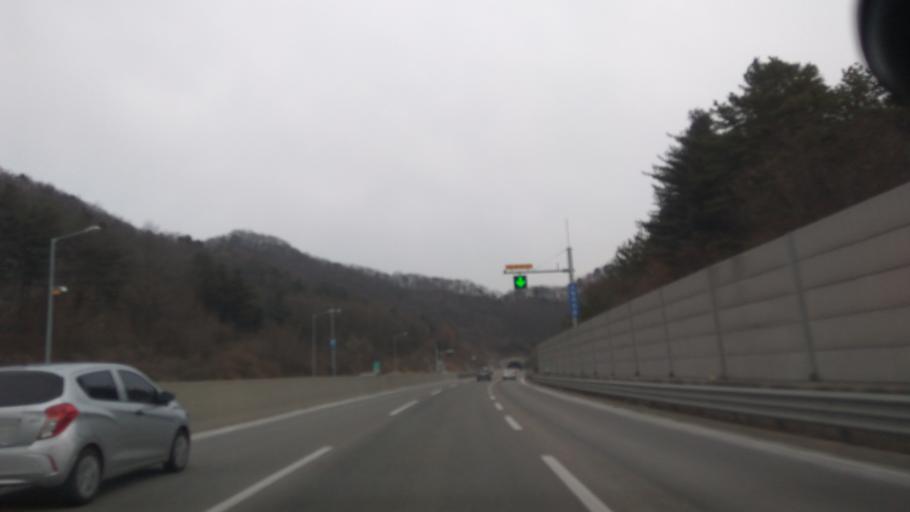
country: KR
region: Gyeonggi-do
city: Cheongpyeong
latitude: 37.6494
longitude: 127.4296
